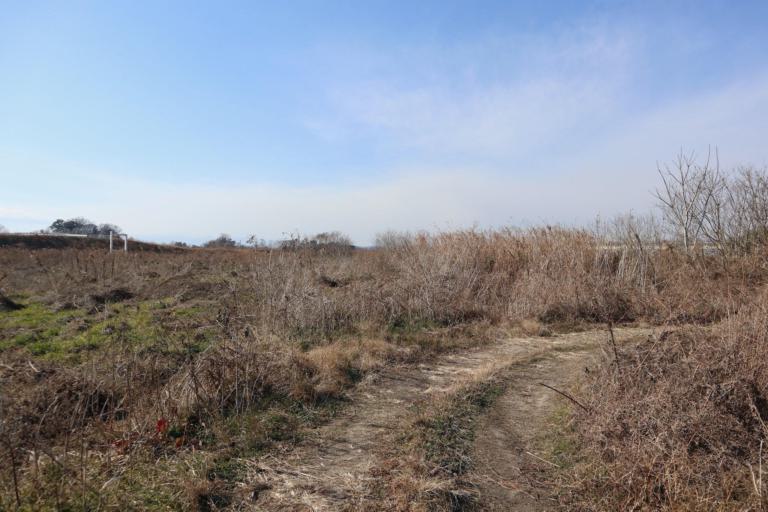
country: JP
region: Saitama
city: Fukiage-fujimi
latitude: 36.0832
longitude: 139.4380
